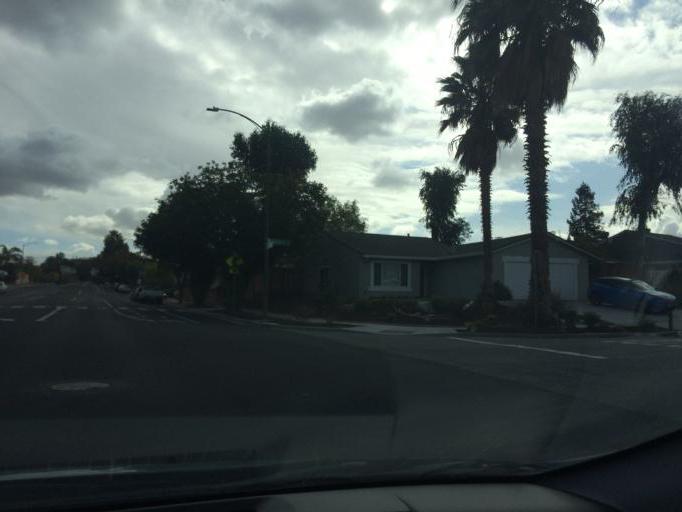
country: US
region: California
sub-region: Santa Clara County
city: Seven Trees
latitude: 37.3067
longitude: -121.7980
